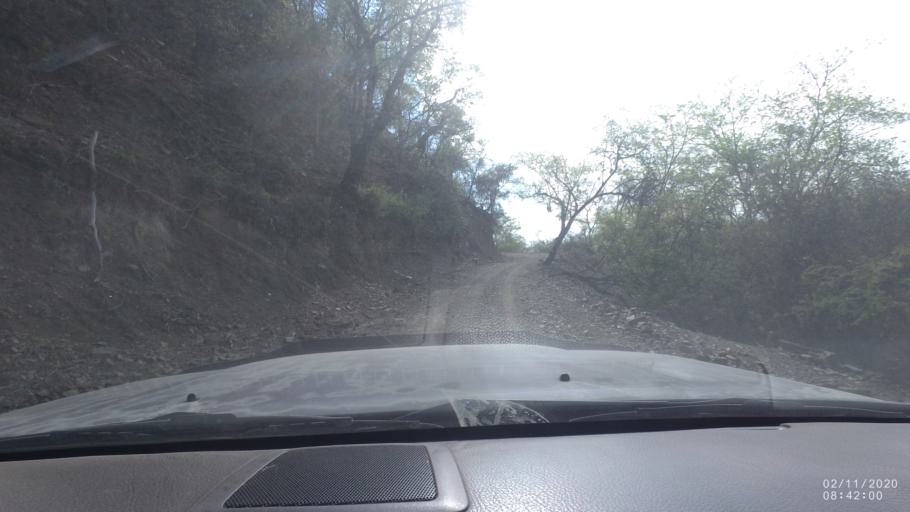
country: BO
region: Chuquisaca
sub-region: Provincia Zudanez
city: Mojocoya
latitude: -18.5769
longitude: -64.5504
